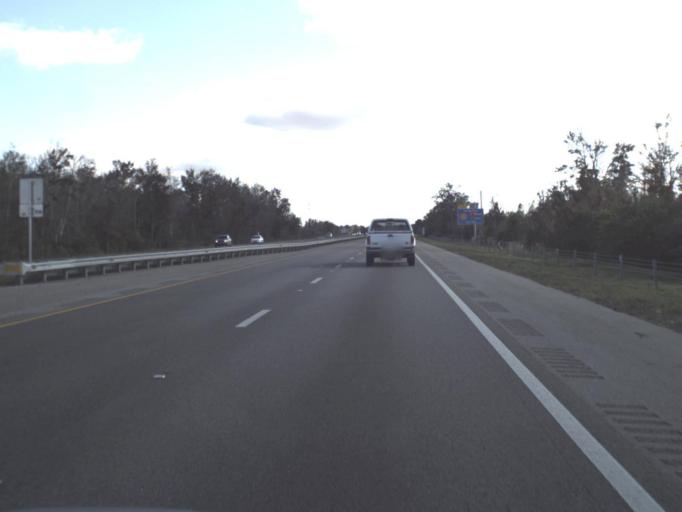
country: US
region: Florida
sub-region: Osceola County
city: Saint Cloud
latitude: 28.1142
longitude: -81.2833
